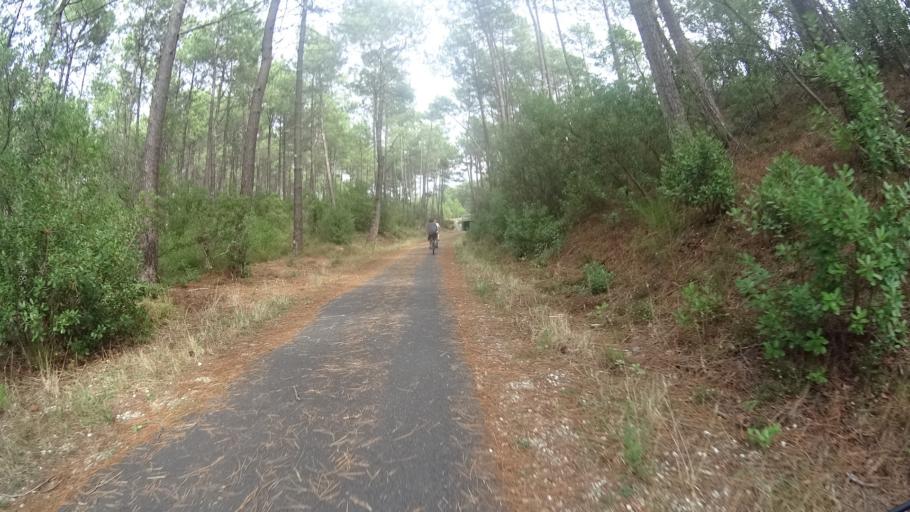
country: FR
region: Aquitaine
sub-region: Departement de la Gironde
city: Lacanau
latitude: 45.0074
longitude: -1.1454
